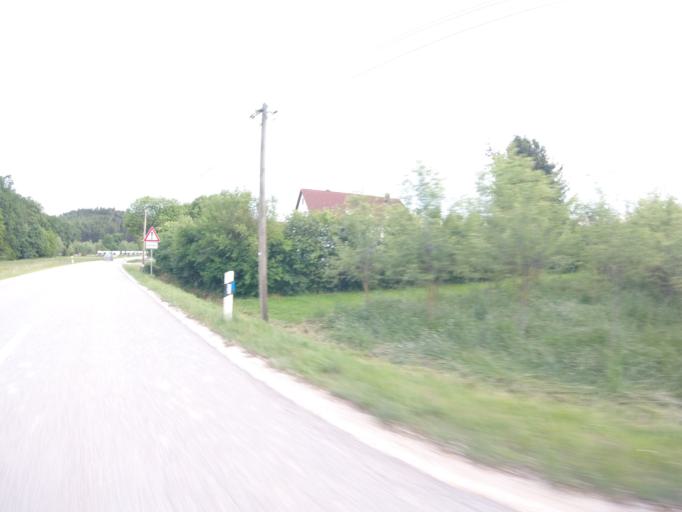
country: DE
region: Bavaria
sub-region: Upper Bavaria
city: Kirchdorf
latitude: 48.4873
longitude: 11.6715
